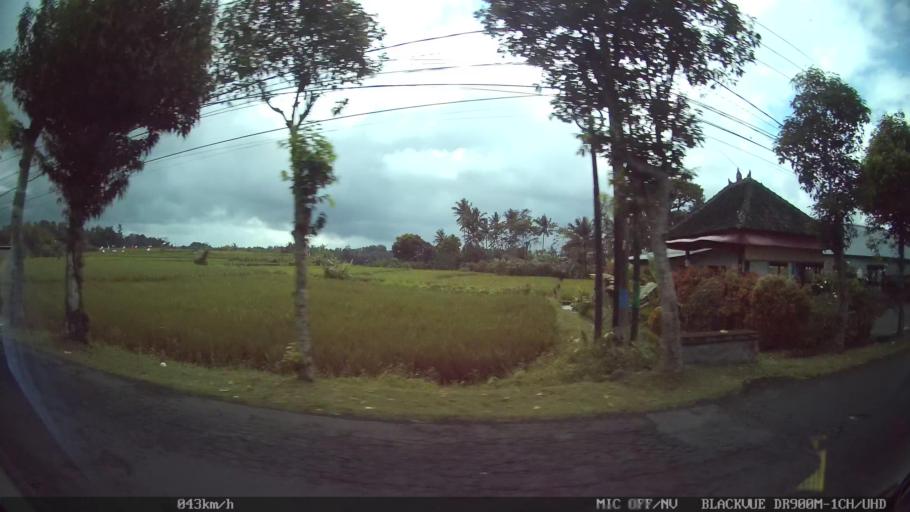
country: ID
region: Bali
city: Banjar Keraman
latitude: -8.5377
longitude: 115.2143
